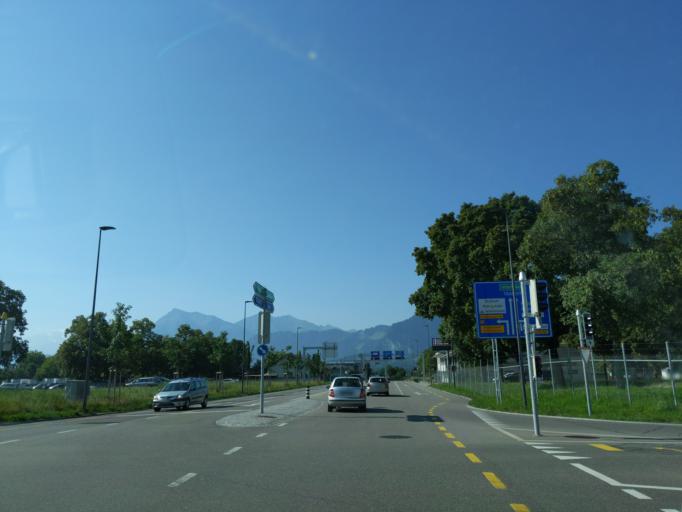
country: CH
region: Bern
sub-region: Thun District
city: Thun
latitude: 46.7626
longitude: 7.6080
